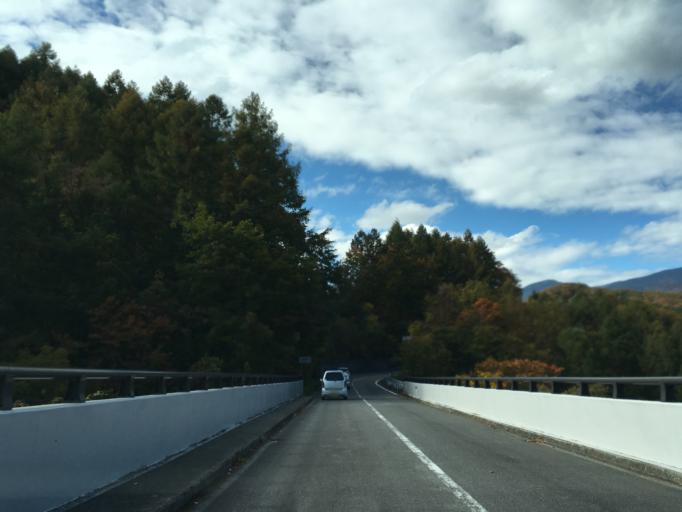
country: JP
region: Fukushima
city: Inawashiro
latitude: 37.6726
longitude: 140.1472
